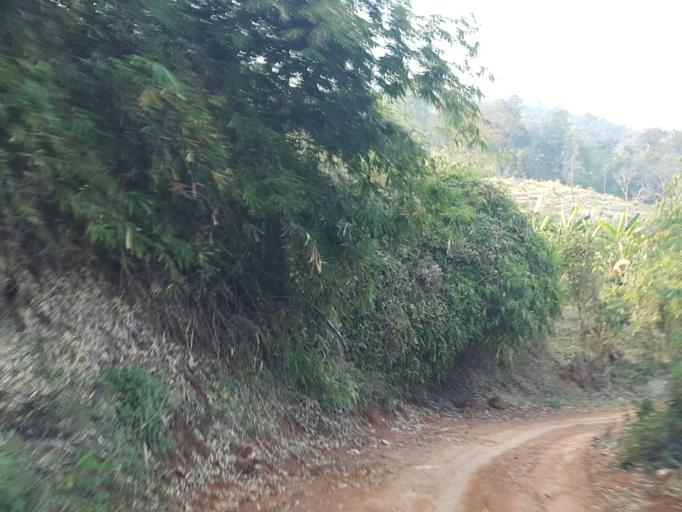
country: TH
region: Chiang Mai
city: Mae Taeng
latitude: 19.0536
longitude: 98.7659
